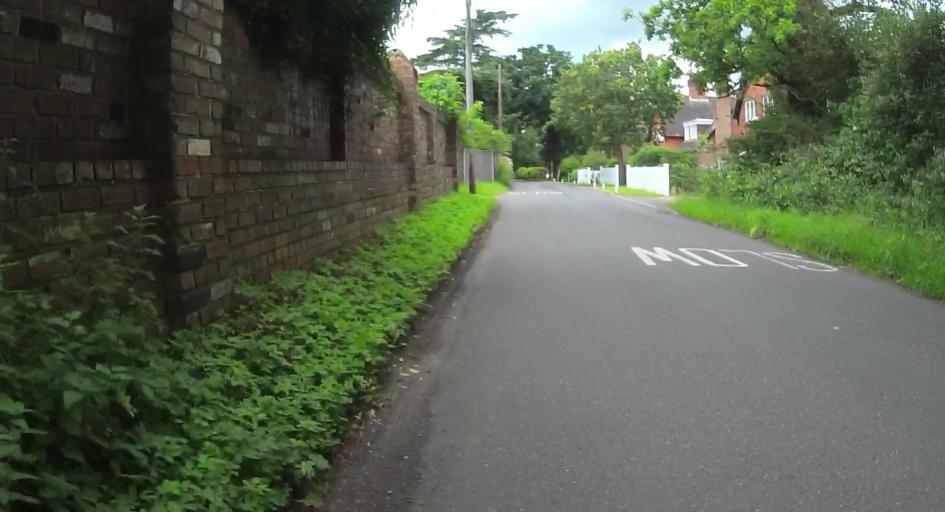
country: GB
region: England
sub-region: Wokingham
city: Wokingham
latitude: 51.3923
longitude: -0.8126
